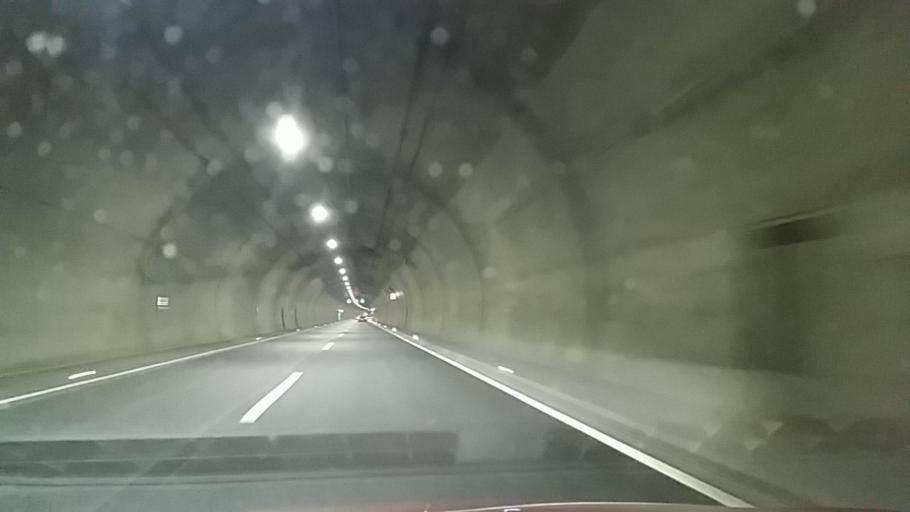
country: DE
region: Thuringia
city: Zella-Mehlis
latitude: 50.6304
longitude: 10.6669
